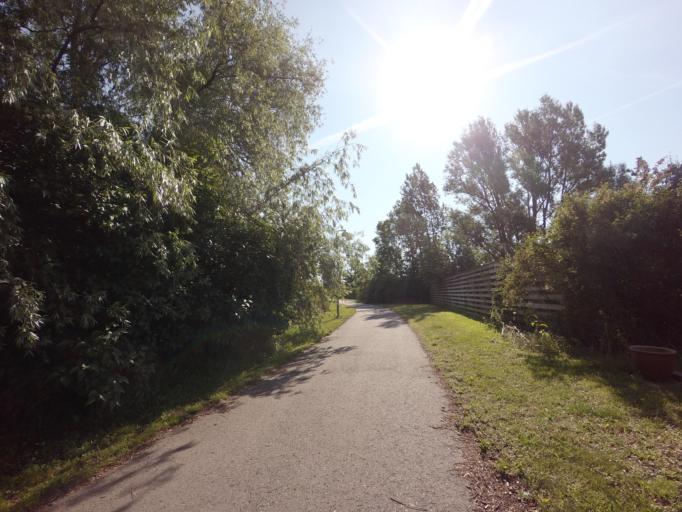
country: SE
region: Skane
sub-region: Malmo
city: Oxie
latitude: 55.4947
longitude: 13.1065
